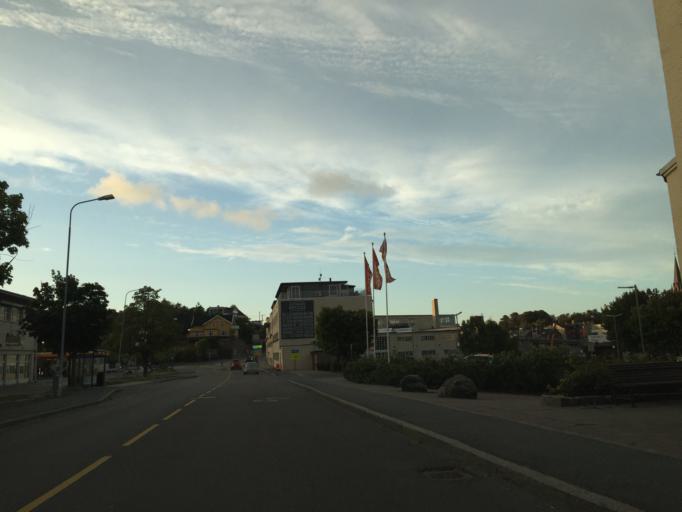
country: NO
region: Ostfold
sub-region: Fredrikstad
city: Fredrikstad
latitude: 59.2054
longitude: 10.9379
